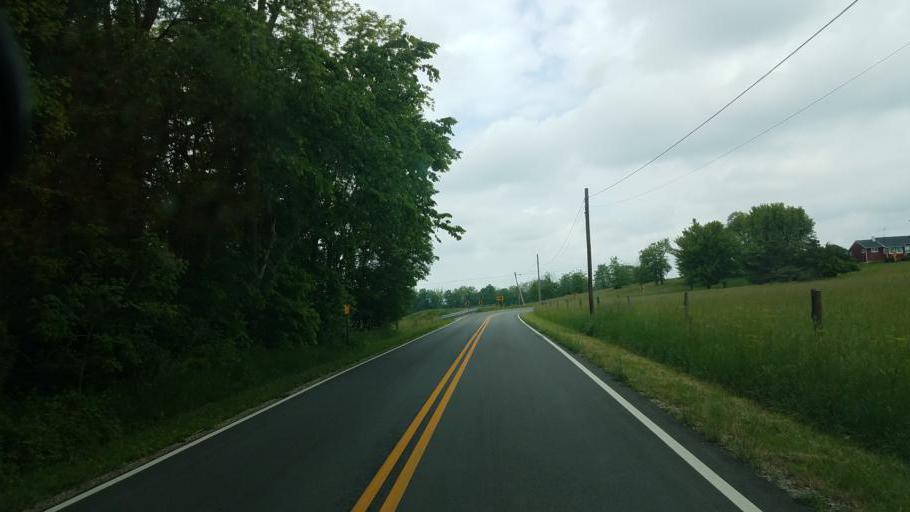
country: US
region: Ohio
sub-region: Delaware County
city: Delaware
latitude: 40.3106
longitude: -83.1684
